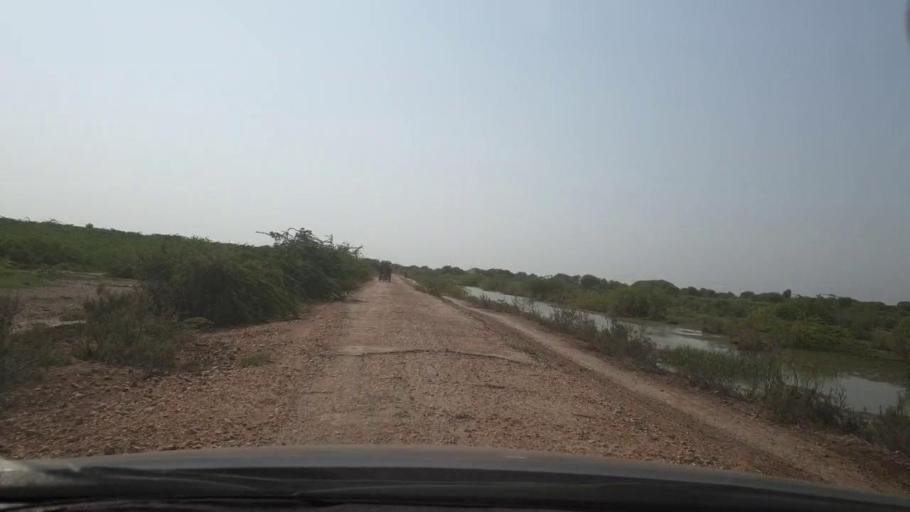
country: PK
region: Sindh
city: Naukot
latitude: 24.7959
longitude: 69.2286
